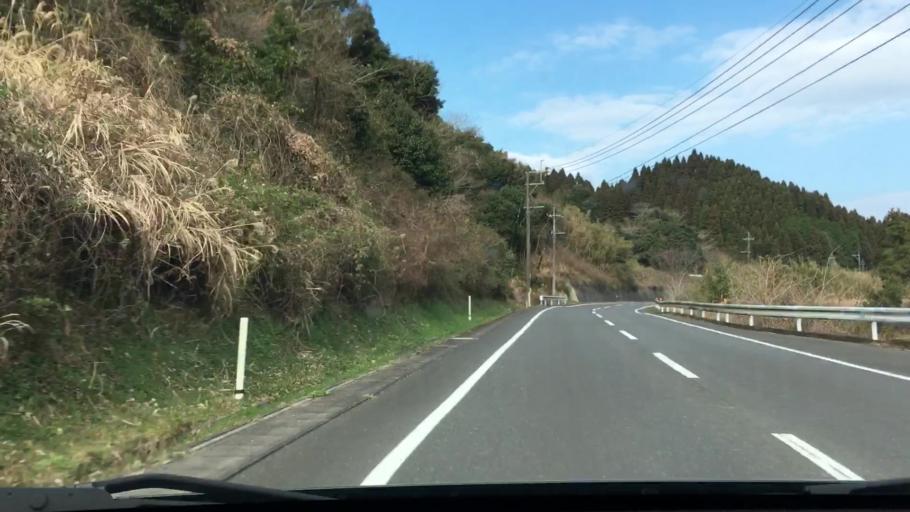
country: JP
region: Miyazaki
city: Kushima
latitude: 31.5733
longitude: 131.2652
